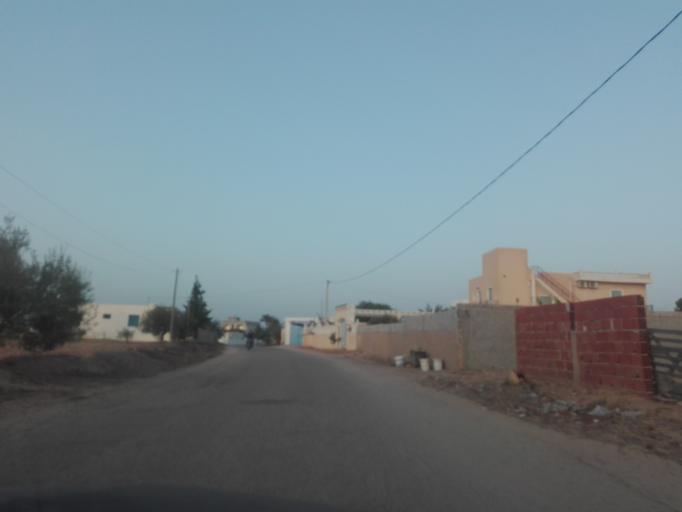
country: TN
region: Madanin
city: Houmt Souk
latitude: 33.7298
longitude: 10.7490
